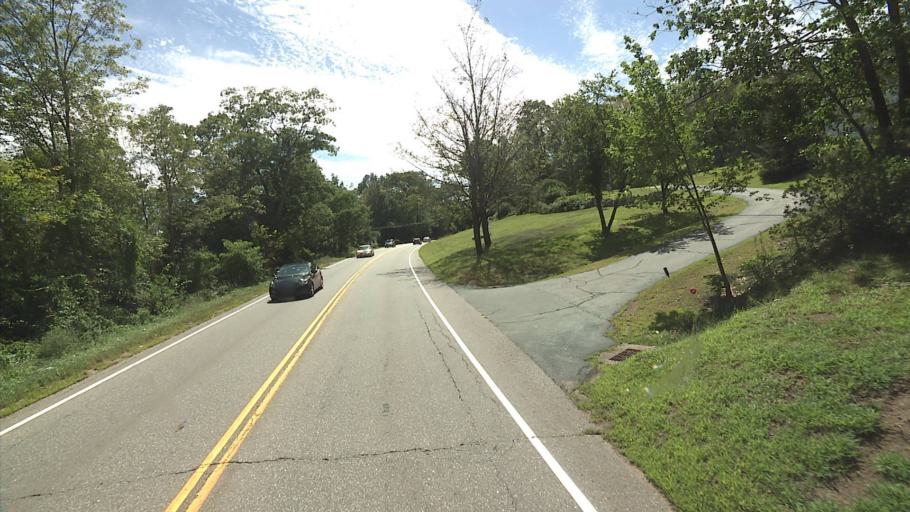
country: US
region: Connecticut
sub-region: Windham County
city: Willimantic
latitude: 41.7511
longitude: -72.1917
